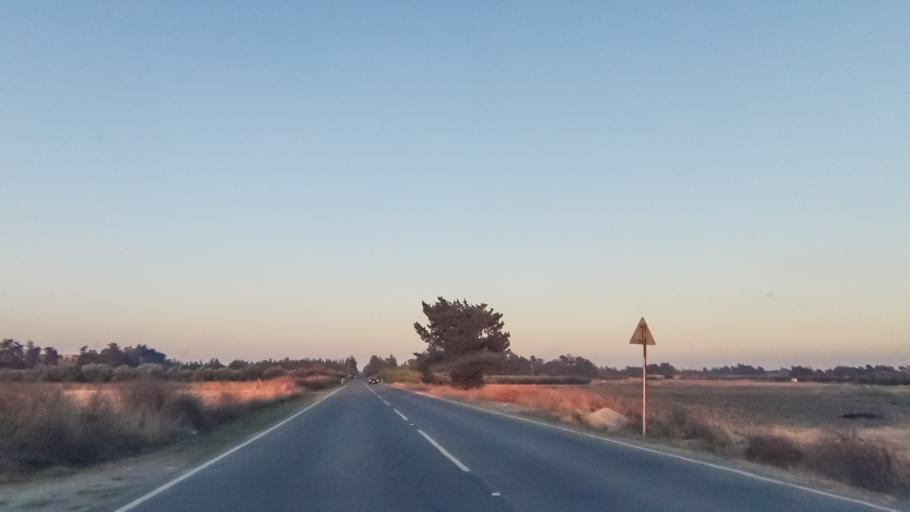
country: CY
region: Limassol
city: Erimi
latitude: 34.6616
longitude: 32.8984
